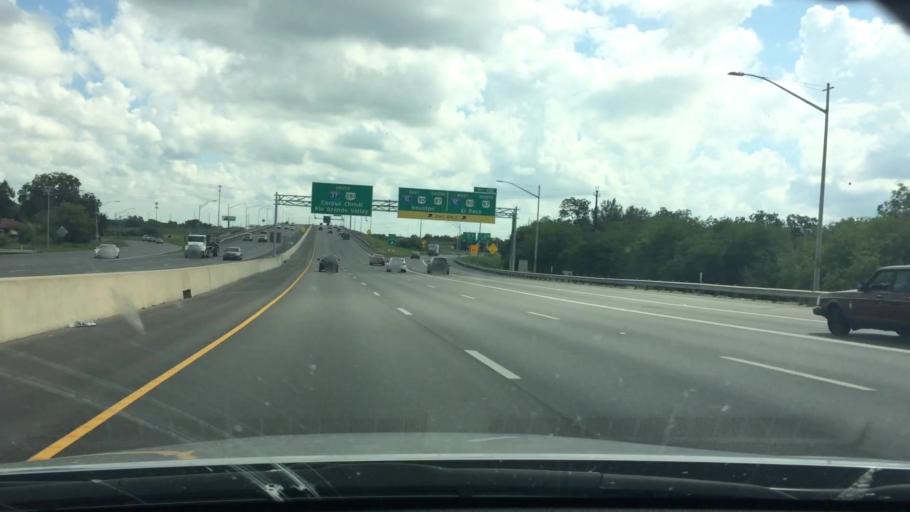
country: US
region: Texas
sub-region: Bexar County
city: San Antonio
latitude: 29.4002
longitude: -98.4805
